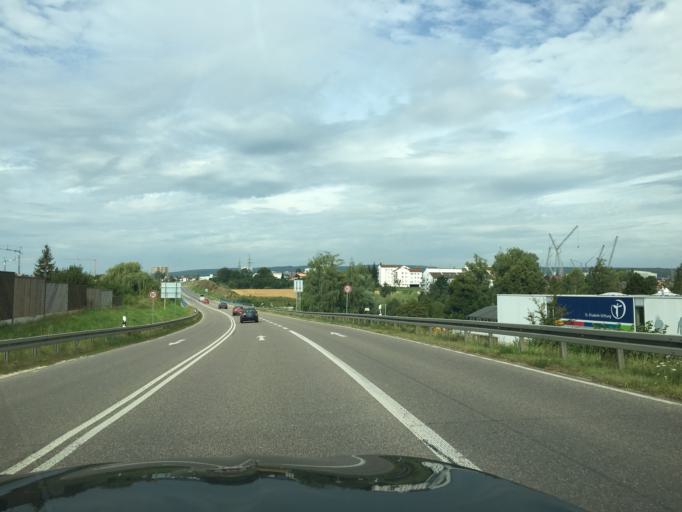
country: DE
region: Baden-Wuerttemberg
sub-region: Tuebingen Region
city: Ehingen
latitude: 48.2903
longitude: 9.7298
